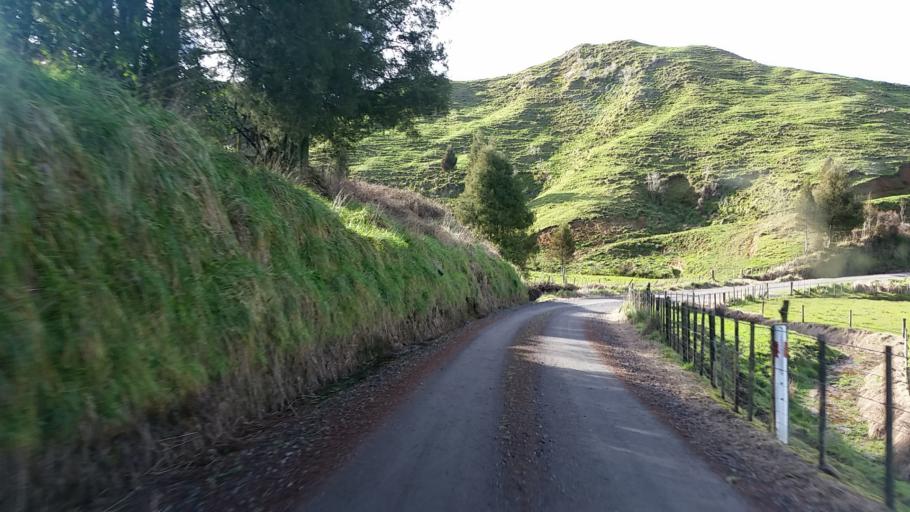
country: NZ
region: Taranaki
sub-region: South Taranaki District
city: Eltham
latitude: -39.2552
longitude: 174.5231
